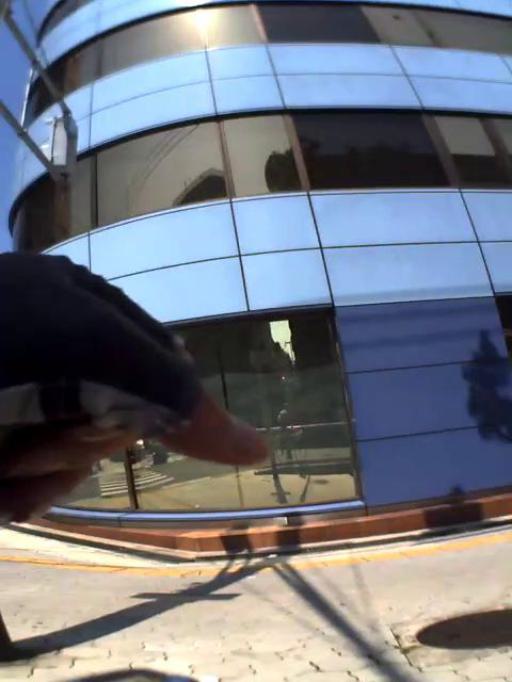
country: JP
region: Osaka
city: Osaka-shi
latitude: 34.6674
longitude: 135.5158
